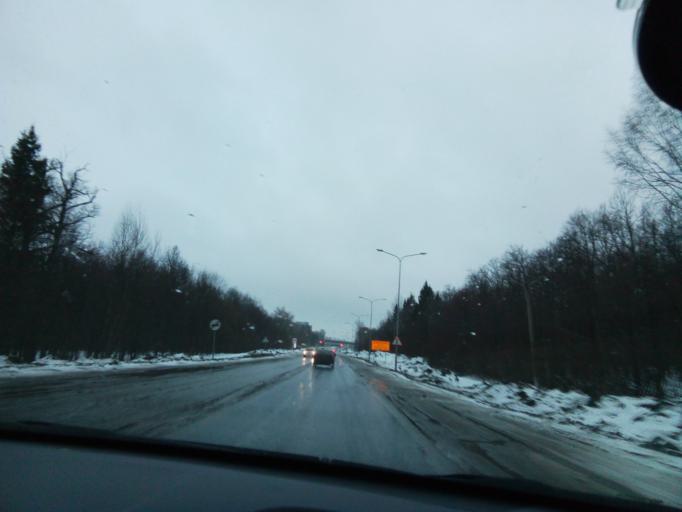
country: RU
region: Chuvashia
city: Novyye Lapsary
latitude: 56.1340
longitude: 47.1715
